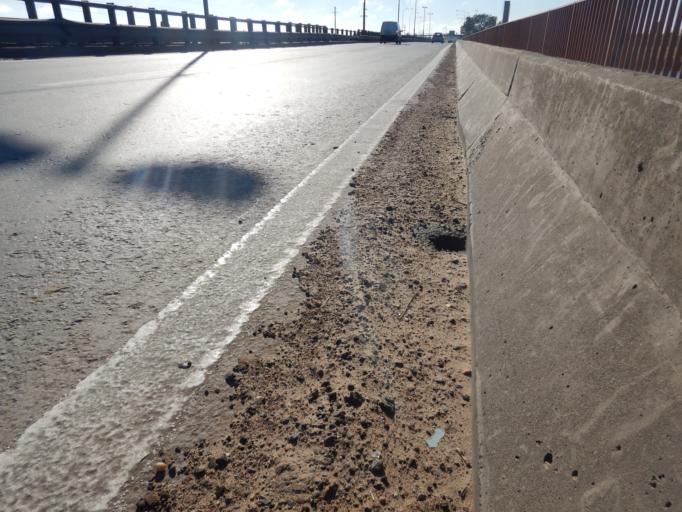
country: AR
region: Santa Fe
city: Santa Fe de la Vera Cruz
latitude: -31.6401
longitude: -60.6382
